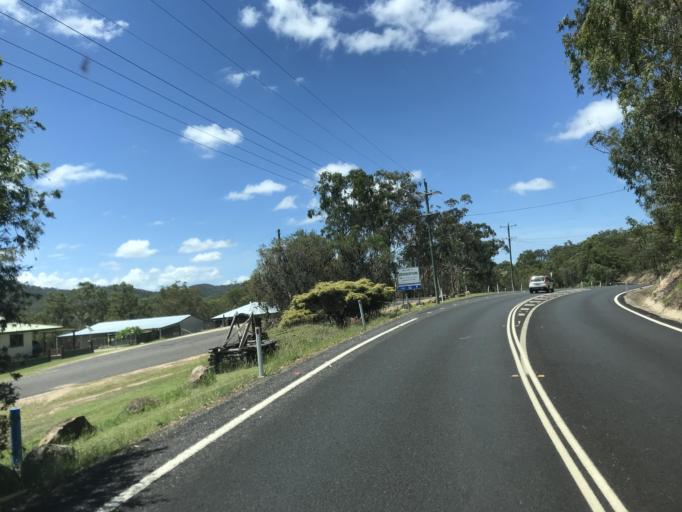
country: AU
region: Queensland
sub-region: Tablelands
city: Atherton
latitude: -17.3969
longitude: 145.3883
